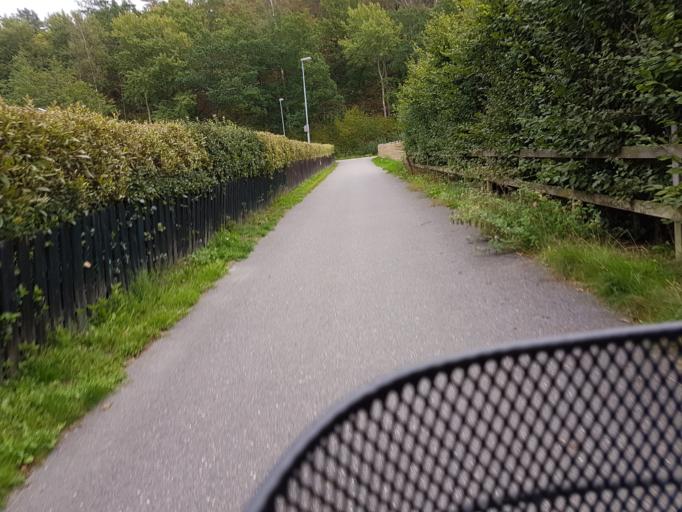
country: SE
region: Vaestra Goetaland
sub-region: Ale Kommun
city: Nodinge-Nol
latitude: 57.9050
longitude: 12.0593
